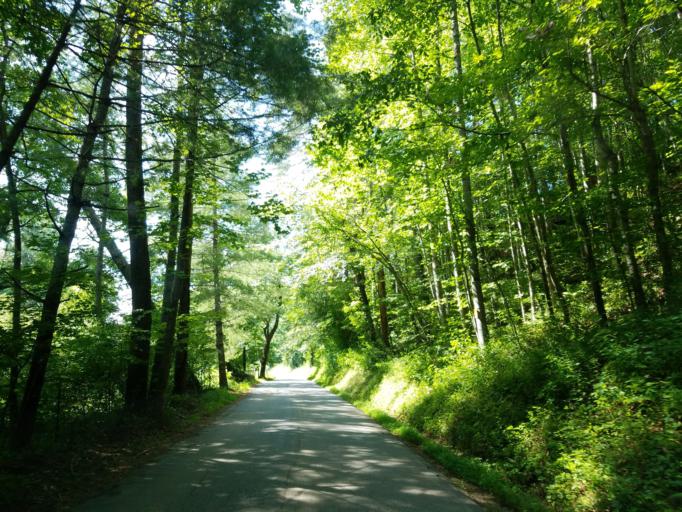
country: US
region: Georgia
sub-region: Dawson County
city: Dawsonville
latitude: 34.5660
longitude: -84.1467
